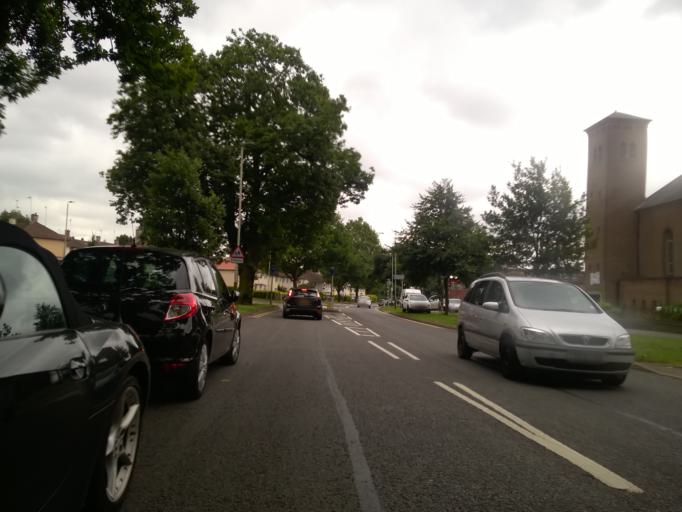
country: GB
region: England
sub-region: City of Leicester
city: Leicester
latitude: 52.6587
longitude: -1.1424
